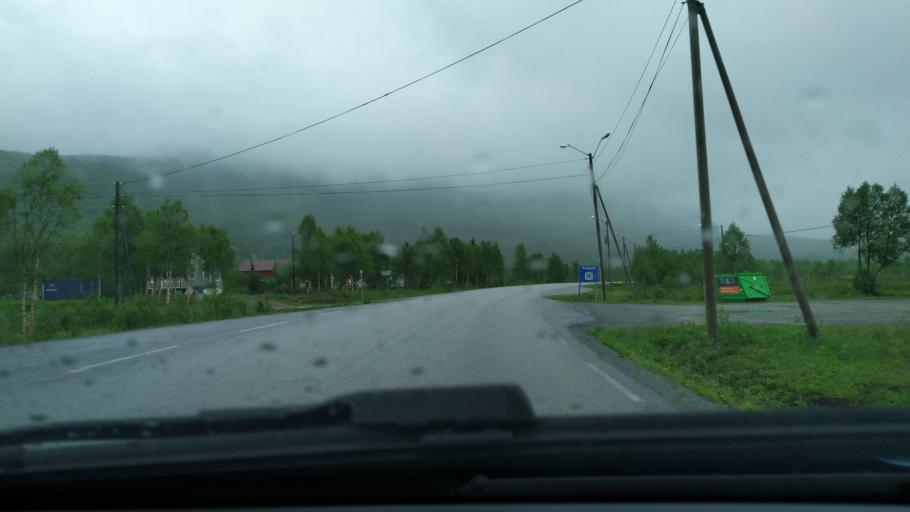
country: NO
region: Troms
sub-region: Dyroy
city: Brostadbotn
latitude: 69.0326
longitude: 17.7380
